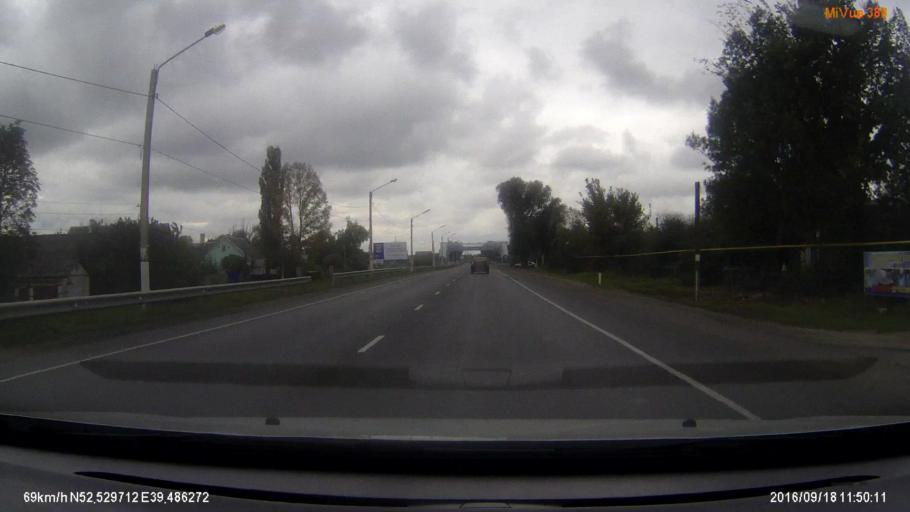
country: RU
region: Lipetsk
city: Syrskoye
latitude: 52.5298
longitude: 39.4865
